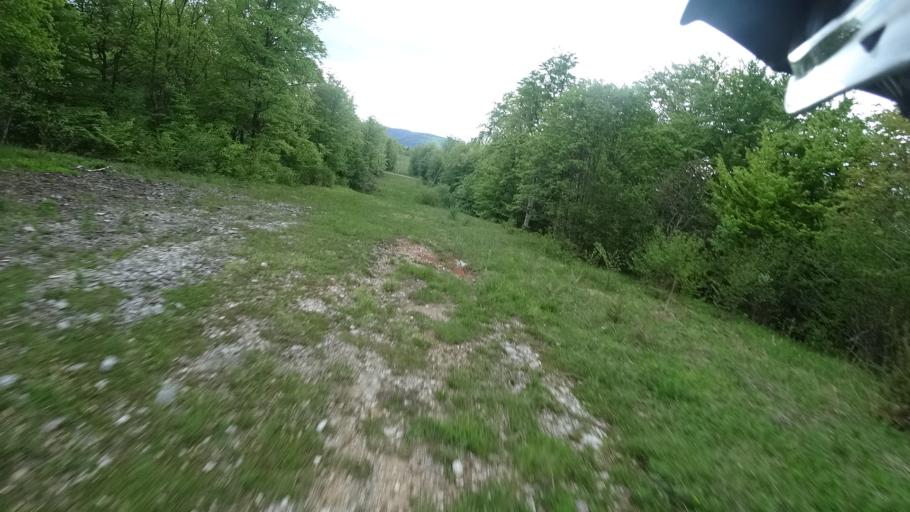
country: HR
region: Karlovacka
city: Plaski
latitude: 44.9068
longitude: 15.4172
